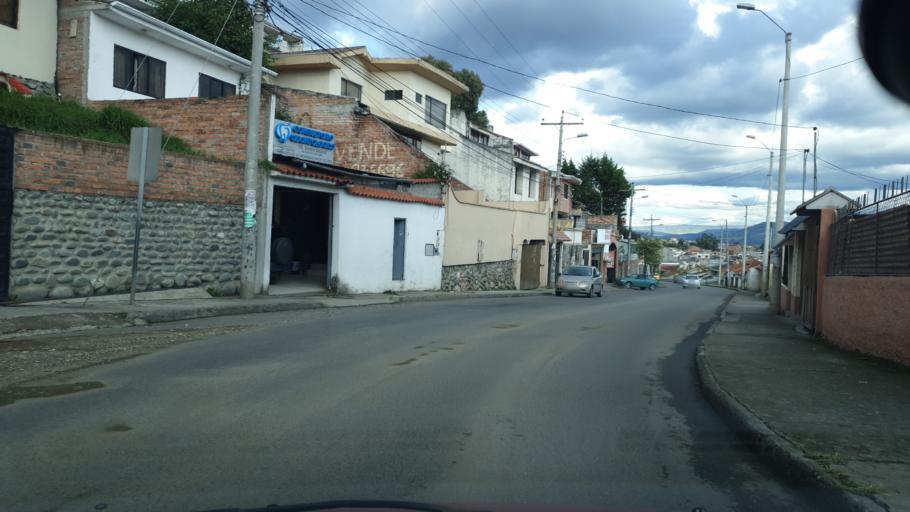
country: EC
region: Azuay
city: Cuenca
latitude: -2.8874
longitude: -79.0119
